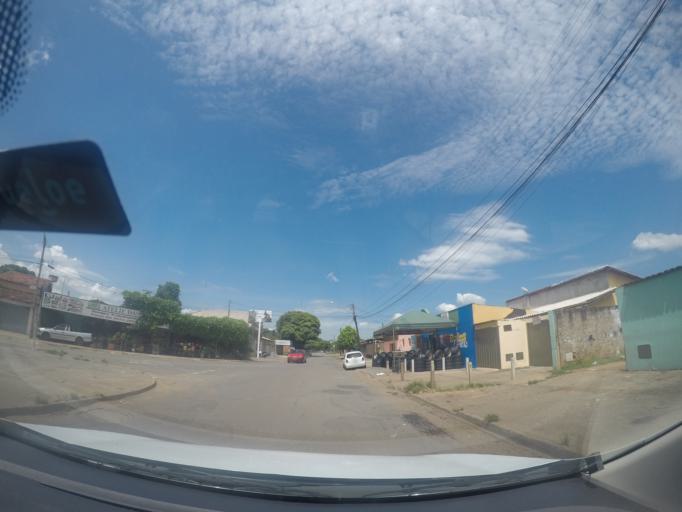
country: BR
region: Goias
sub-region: Goiania
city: Goiania
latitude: -16.6895
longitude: -49.3500
